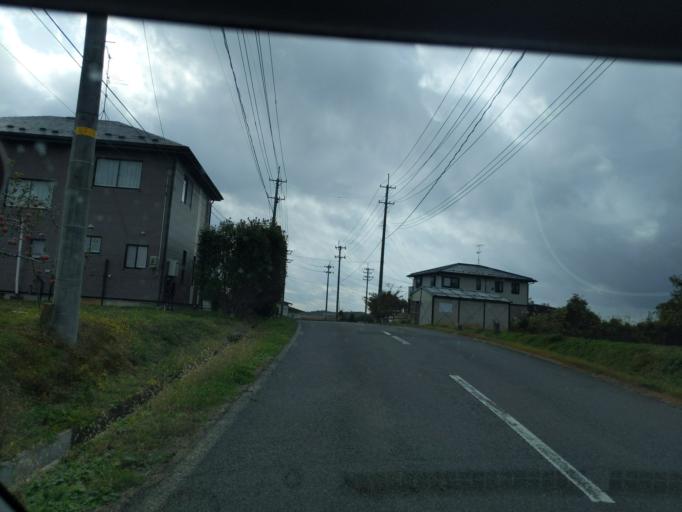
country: JP
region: Iwate
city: Mizusawa
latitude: 39.0599
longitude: 141.1183
